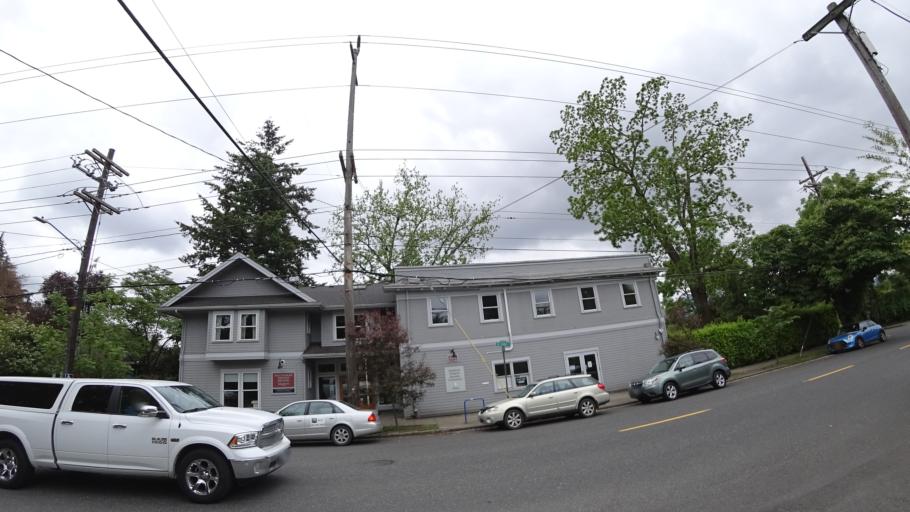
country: US
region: Oregon
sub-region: Multnomah County
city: Portland
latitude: 45.5193
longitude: -122.6174
